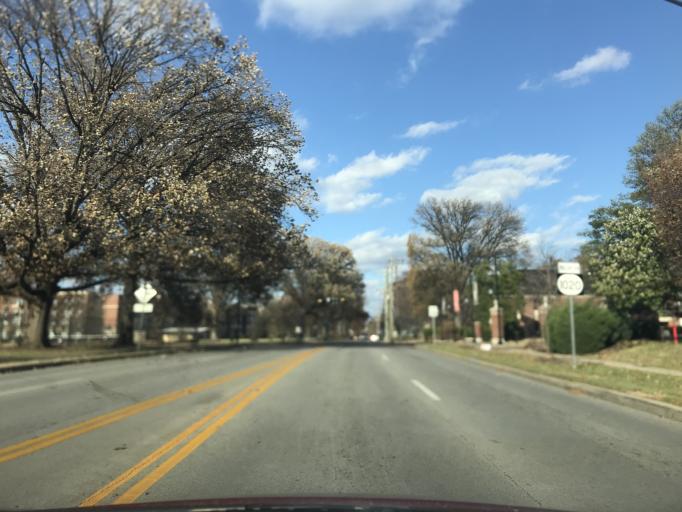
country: US
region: Kentucky
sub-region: Jefferson County
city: Audubon Park
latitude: 38.2147
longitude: -85.7622
